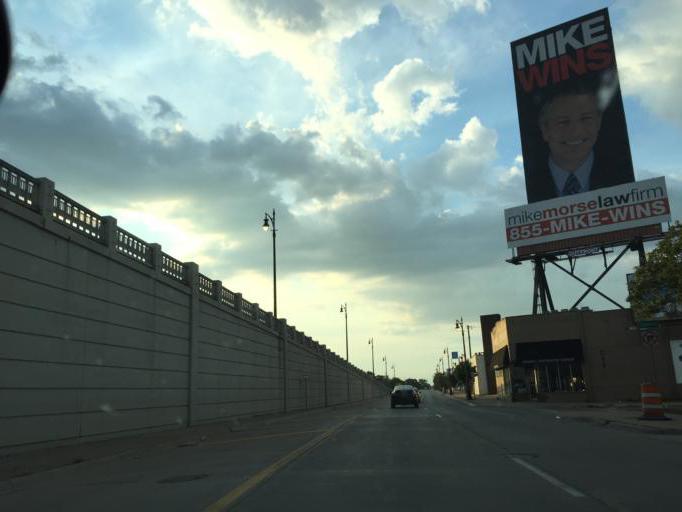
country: US
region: Michigan
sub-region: Oakland County
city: Ferndale
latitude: 42.4469
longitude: -83.1251
